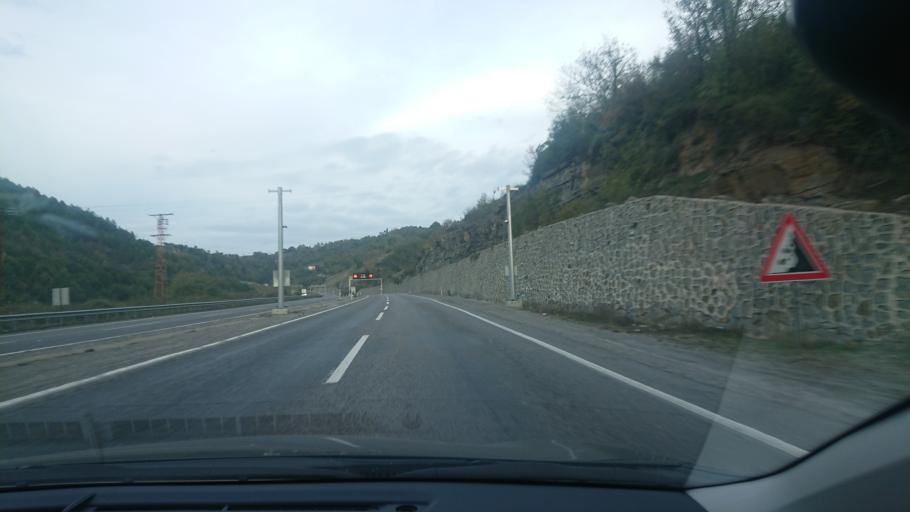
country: TR
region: Zonguldak
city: Beycuma
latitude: 41.4086
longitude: 31.9322
